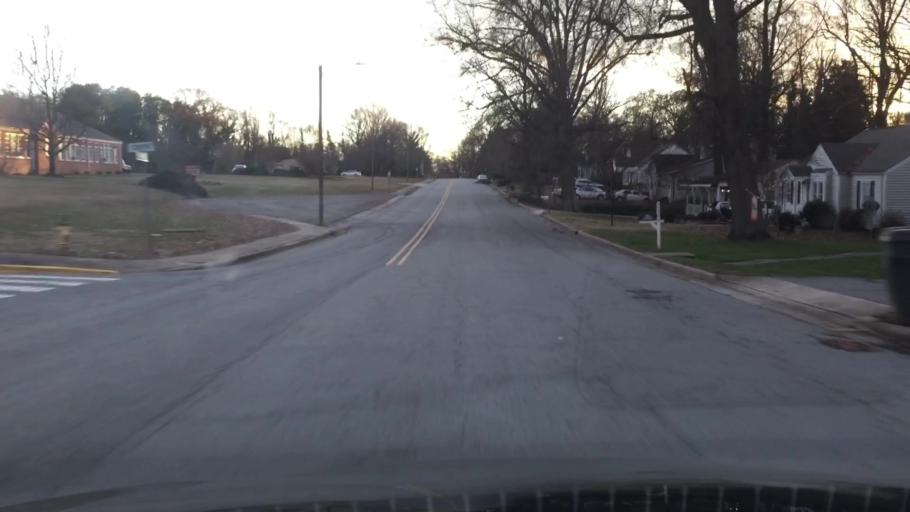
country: US
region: North Carolina
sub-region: Rockingham County
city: Reidsville
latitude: 36.3445
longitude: -79.6680
